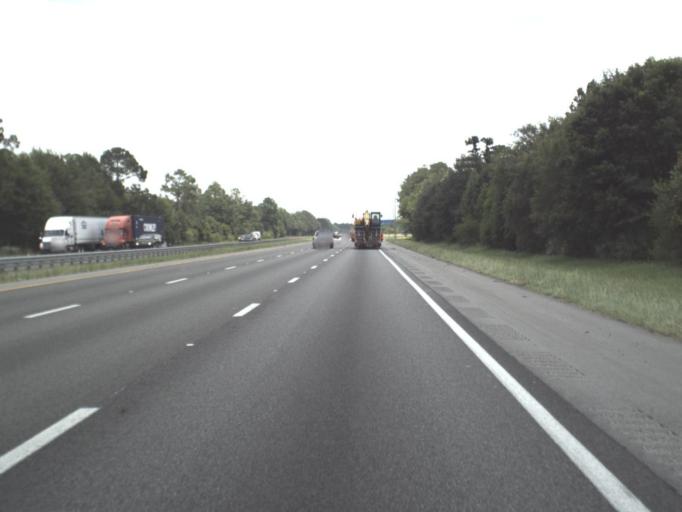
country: US
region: Georgia
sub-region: Echols County
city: Statenville
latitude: 30.6170
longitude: -83.1541
